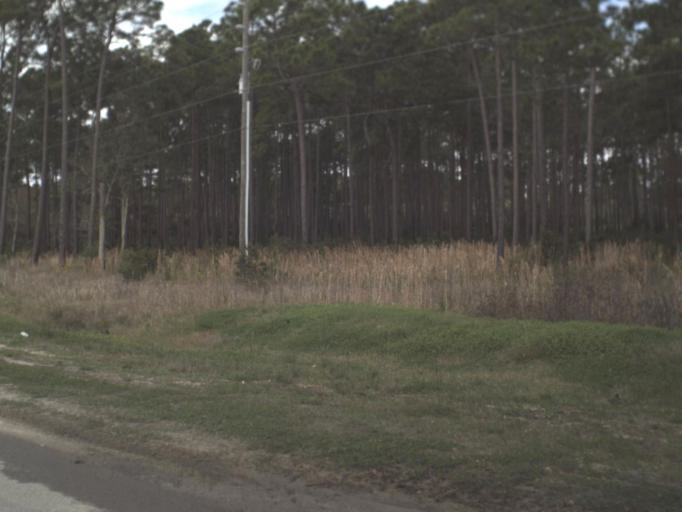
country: US
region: Florida
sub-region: Franklin County
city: Eastpoint
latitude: 29.7623
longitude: -84.8160
